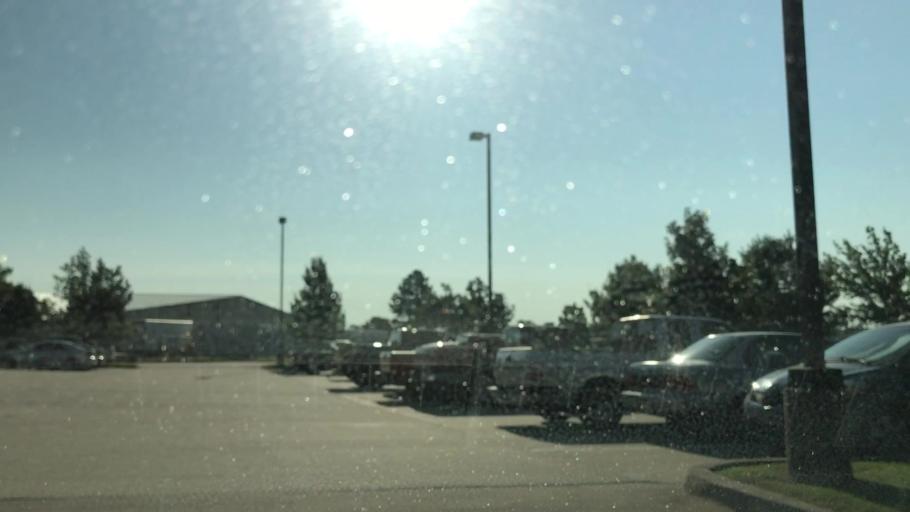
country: US
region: Oklahoma
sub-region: Cleveland County
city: Norman
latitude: 35.2517
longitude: -97.4942
